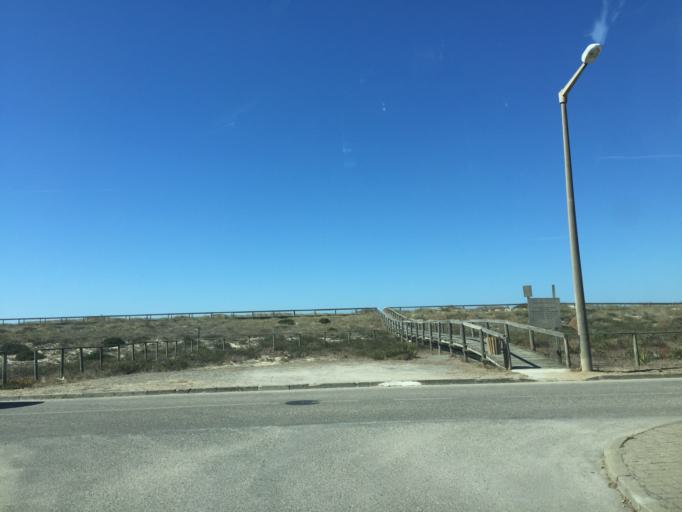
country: PT
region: Coimbra
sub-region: Figueira da Foz
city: Buarcos
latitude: 40.2138
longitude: -8.8938
